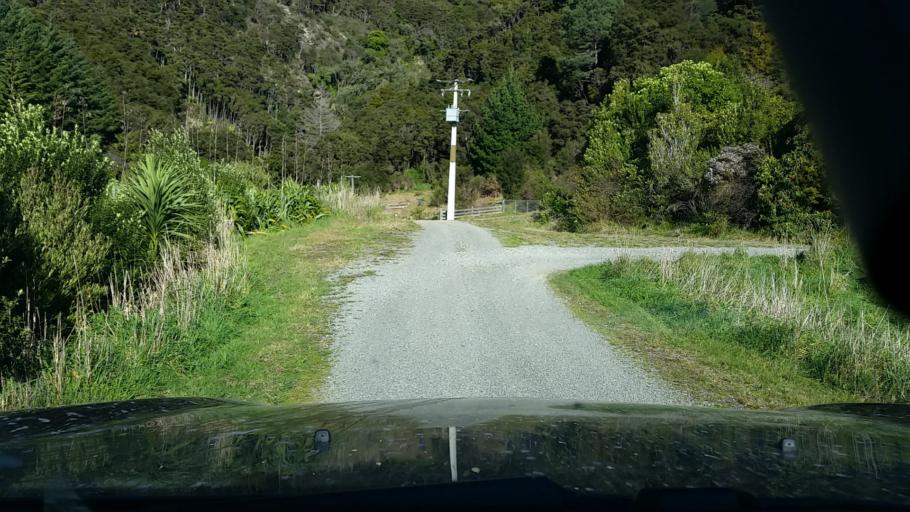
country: NZ
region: Marlborough
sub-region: Marlborough District
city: Picton
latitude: -41.2757
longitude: 173.7379
